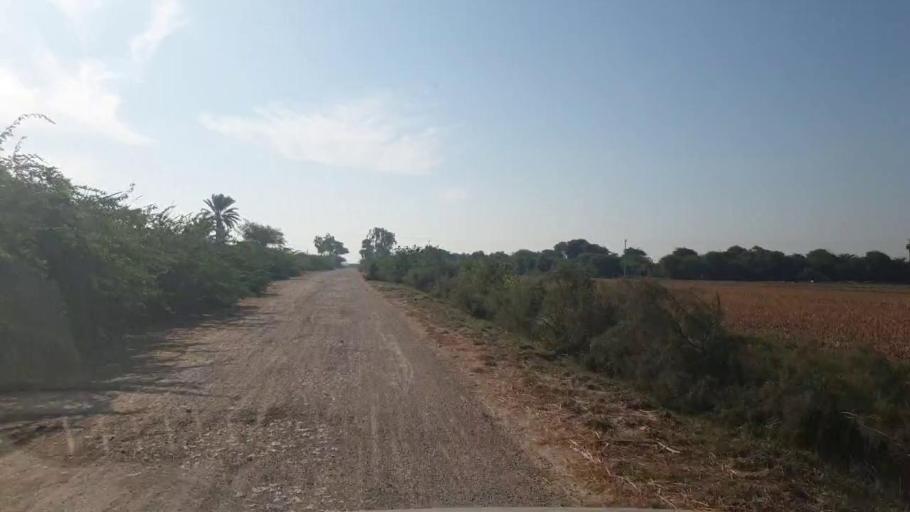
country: PK
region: Sindh
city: Rajo Khanani
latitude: 24.9650
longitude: 68.7958
